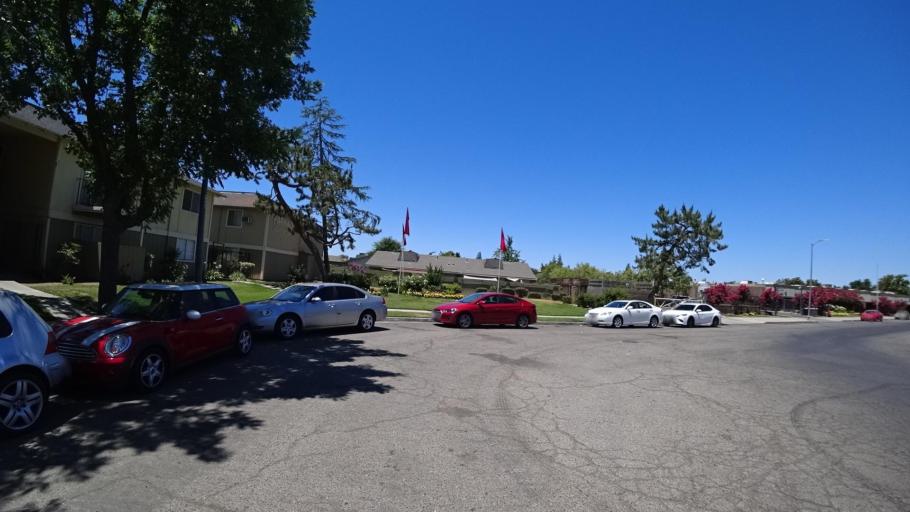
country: US
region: California
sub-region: Fresno County
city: Clovis
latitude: 36.8073
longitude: -119.7583
